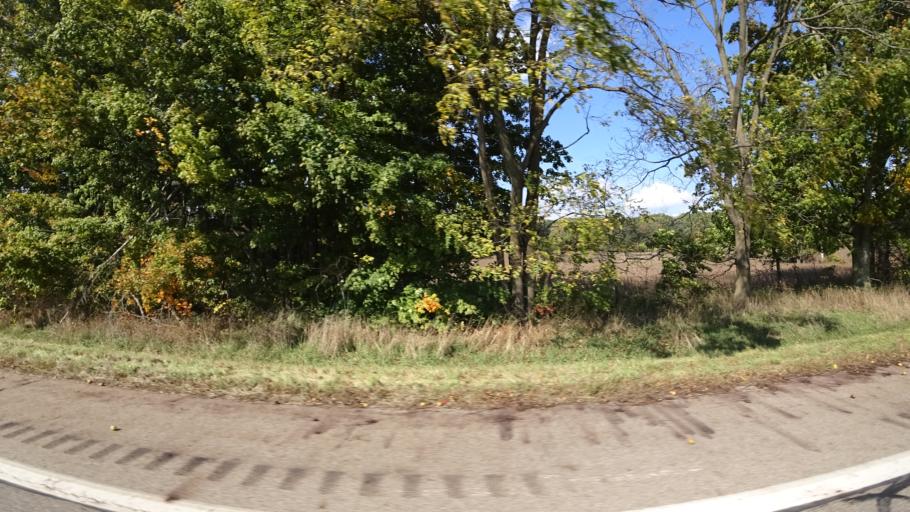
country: US
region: Michigan
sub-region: Calhoun County
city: Homer
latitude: 42.1524
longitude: -84.7884
